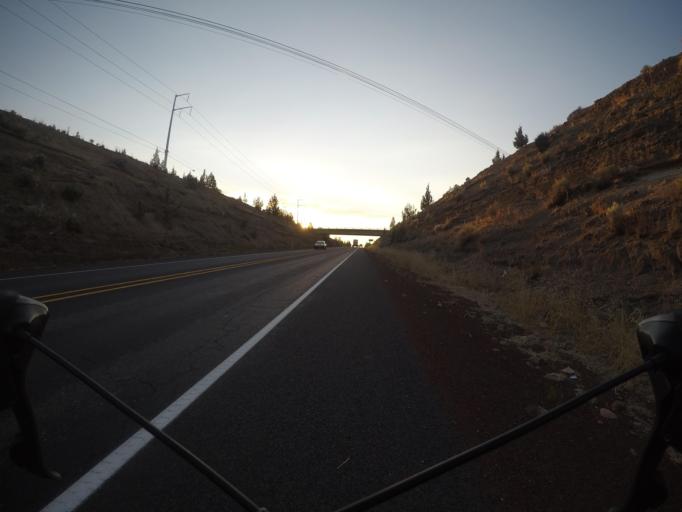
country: US
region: Oregon
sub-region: Deschutes County
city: Redmond
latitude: 44.2747
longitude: -121.2607
